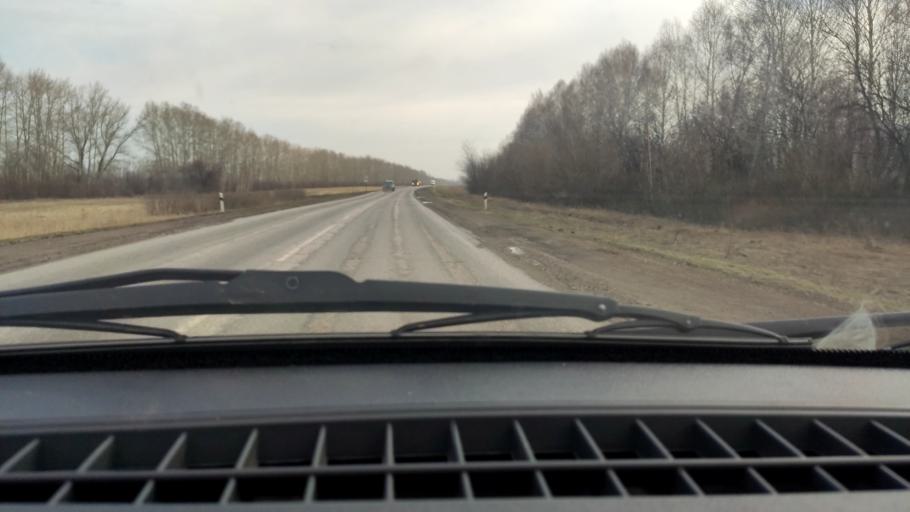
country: RU
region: Bashkortostan
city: Davlekanovo
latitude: 54.3494
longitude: 55.1782
